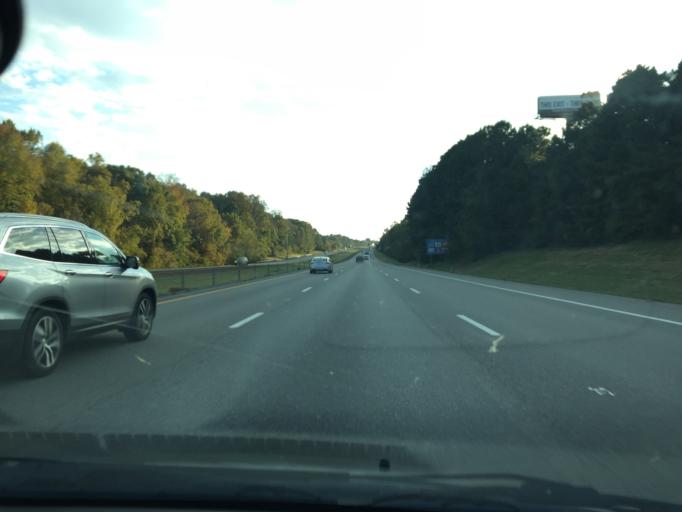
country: US
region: Tennessee
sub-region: Bradley County
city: Hopewell
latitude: 35.2093
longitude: -84.8693
